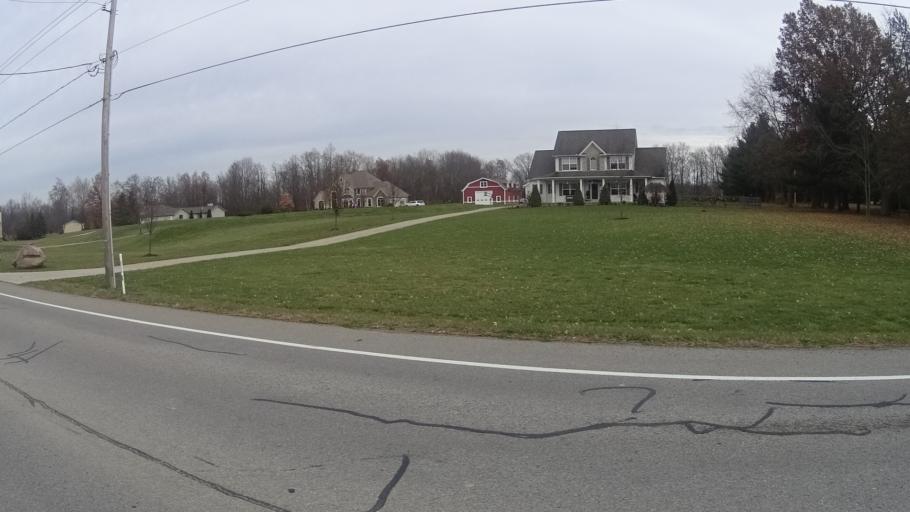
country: US
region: Ohio
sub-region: Lorain County
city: Eaton Estates
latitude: 41.2798
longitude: -81.9565
